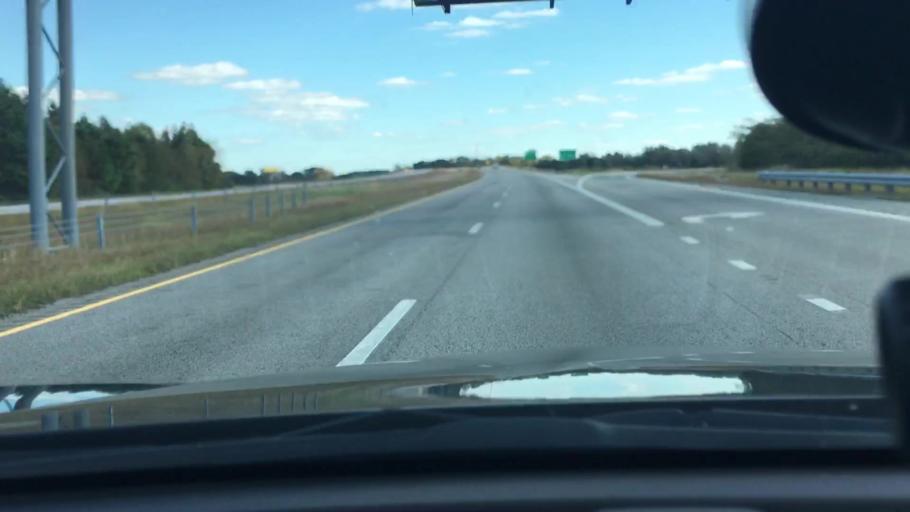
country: US
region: North Carolina
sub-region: Wilson County
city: Wilson
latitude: 35.6812
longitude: -77.9579
